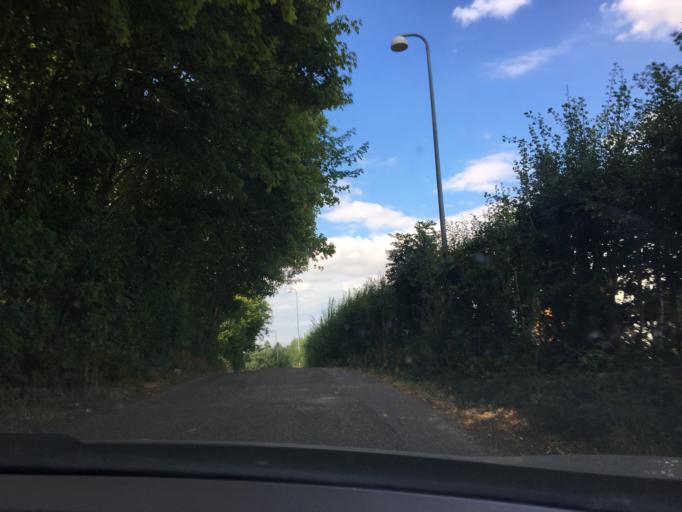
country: DK
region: South Denmark
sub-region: Nordfyns Kommune
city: Sonderso
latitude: 55.4523
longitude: 10.1837
